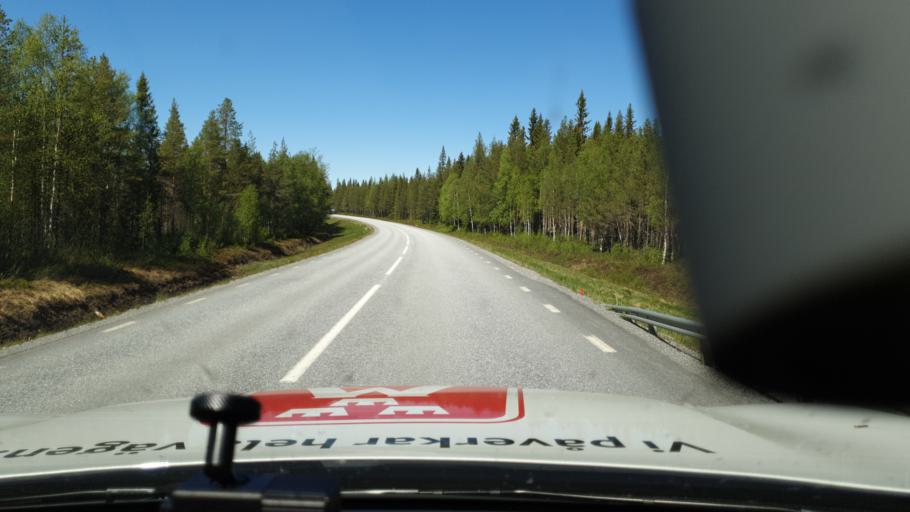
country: SE
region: Vaesterbotten
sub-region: Storumans Kommun
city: Storuman
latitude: 65.2143
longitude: 16.9867
